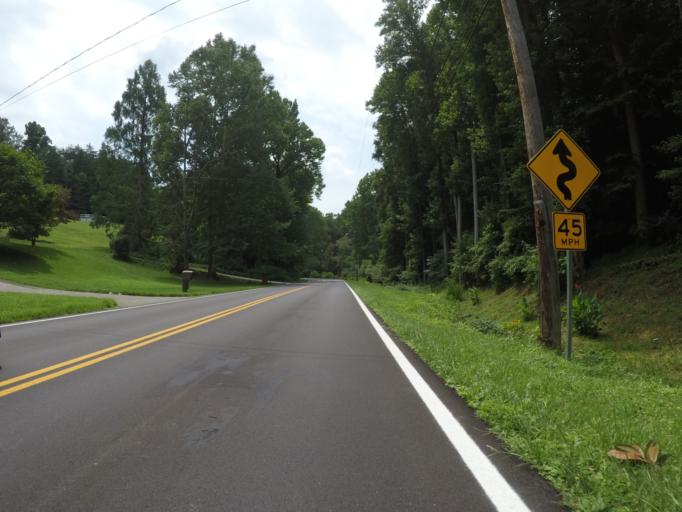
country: US
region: Kentucky
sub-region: Boyd County
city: Ashland
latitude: 38.4451
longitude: -82.6369
